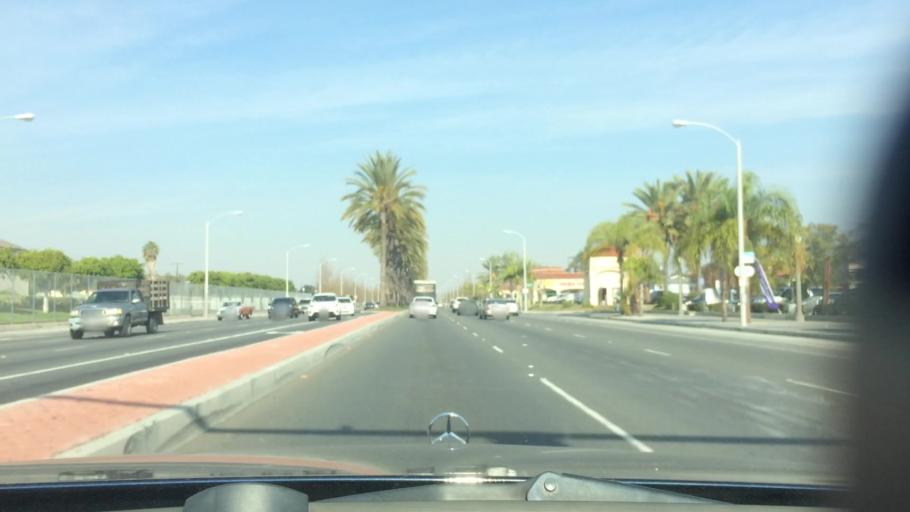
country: US
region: California
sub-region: Orange County
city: Santa Ana
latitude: 33.7347
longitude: -117.8851
